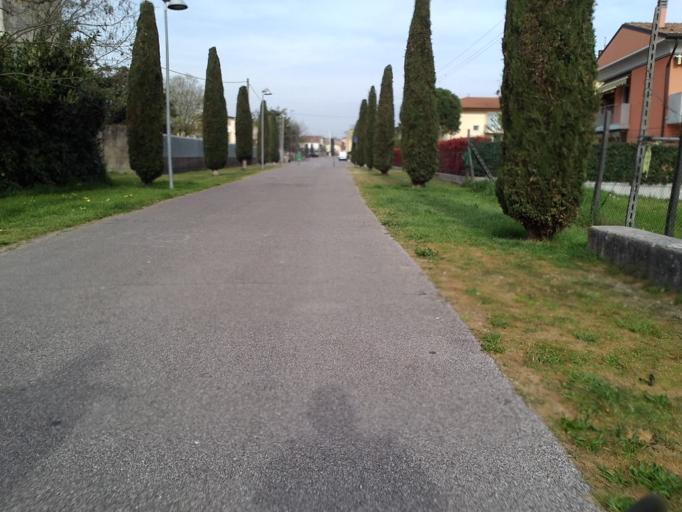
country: IT
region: Veneto
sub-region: Provincia di Verona
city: Villafranca di Verona
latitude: 45.3502
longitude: 10.8526
